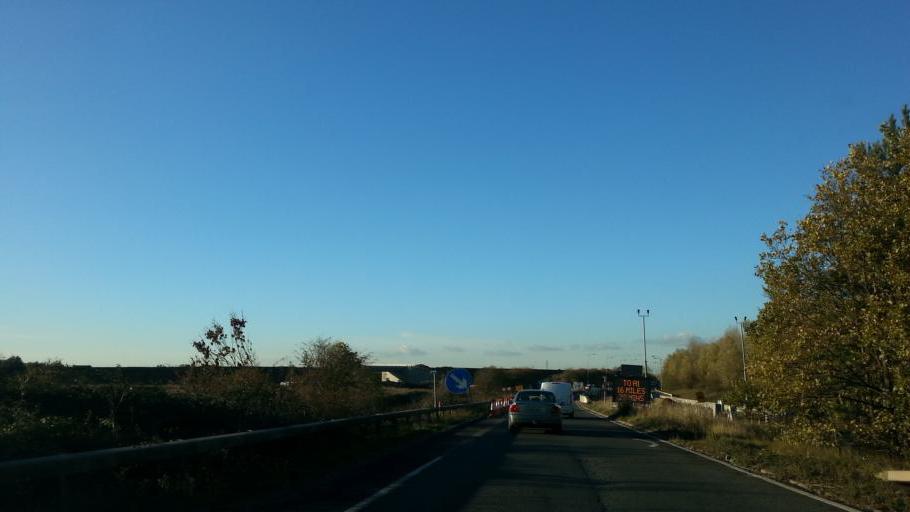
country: GB
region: England
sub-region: Cambridgeshire
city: Girton
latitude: 52.2333
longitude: 0.0672
